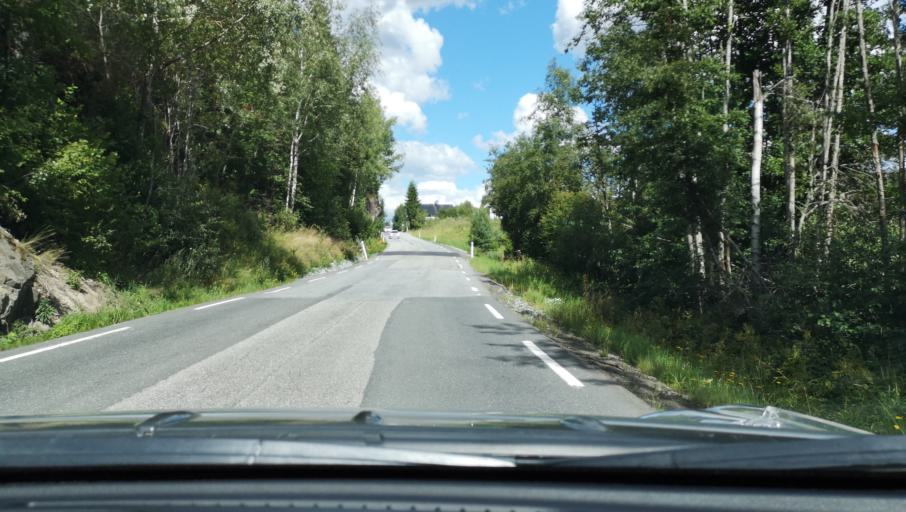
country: NO
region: Ostfold
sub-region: Hobol
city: Elvestad
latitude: 59.6346
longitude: 10.9608
